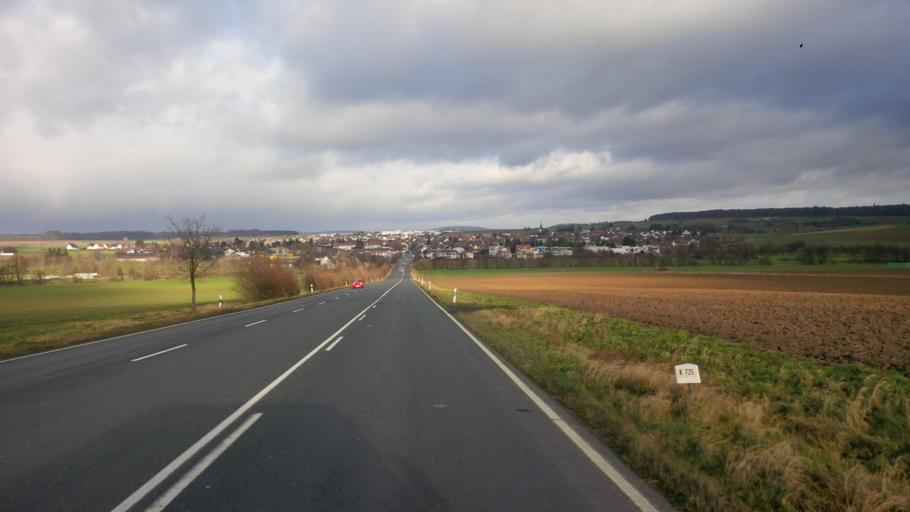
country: DE
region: Hesse
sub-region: Regierungsbezirk Darmstadt
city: Wehrheim
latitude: 50.2872
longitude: 8.5694
